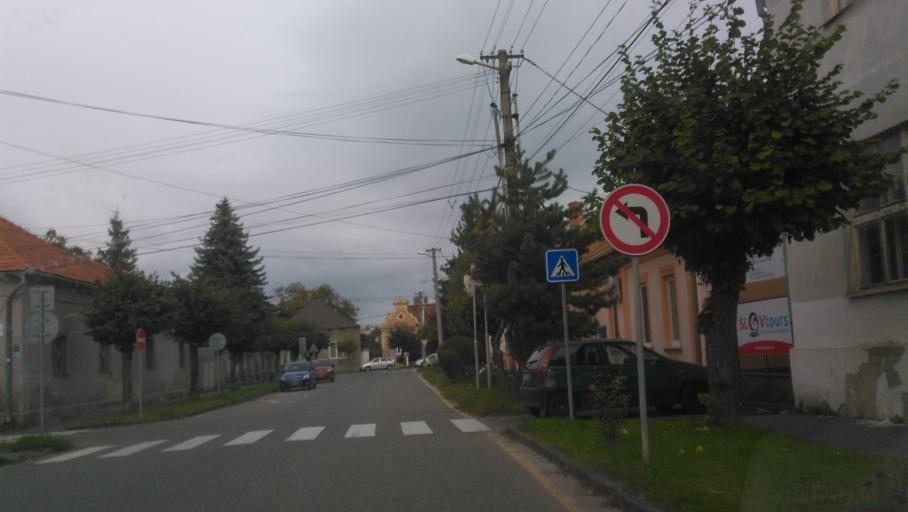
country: SK
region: Banskobystricky
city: Rimavska Sobota
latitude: 48.3857
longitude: 20.0184
